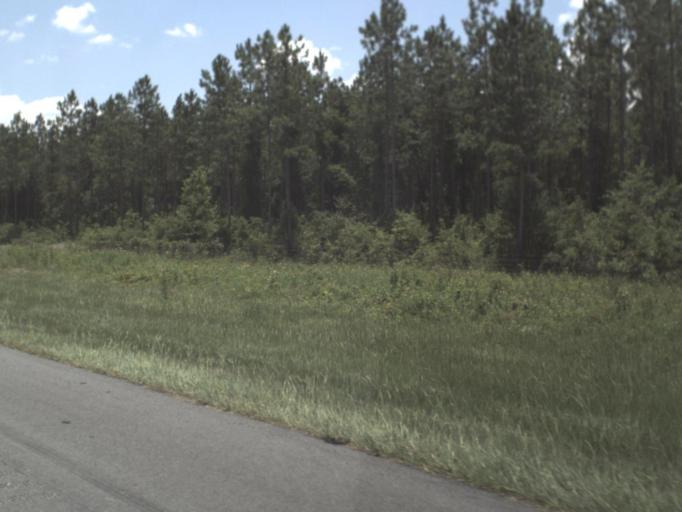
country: US
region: Florida
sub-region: Madison County
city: Madison
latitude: 30.3843
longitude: -83.3137
